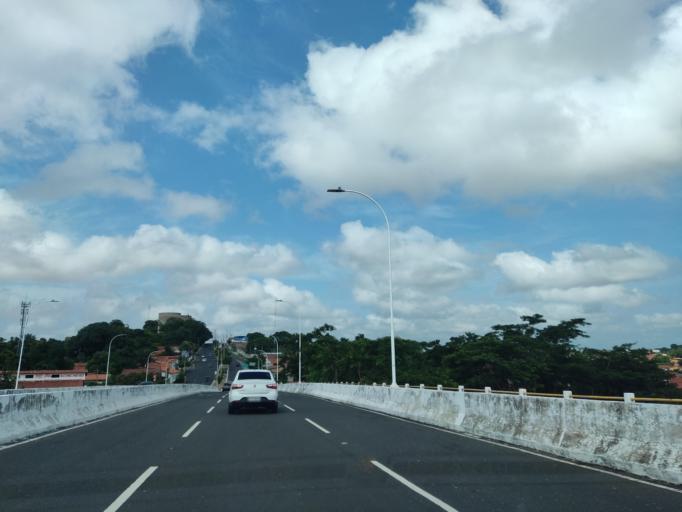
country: BR
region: Piaui
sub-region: Teresina
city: Teresina
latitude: -5.0704
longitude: -42.8038
